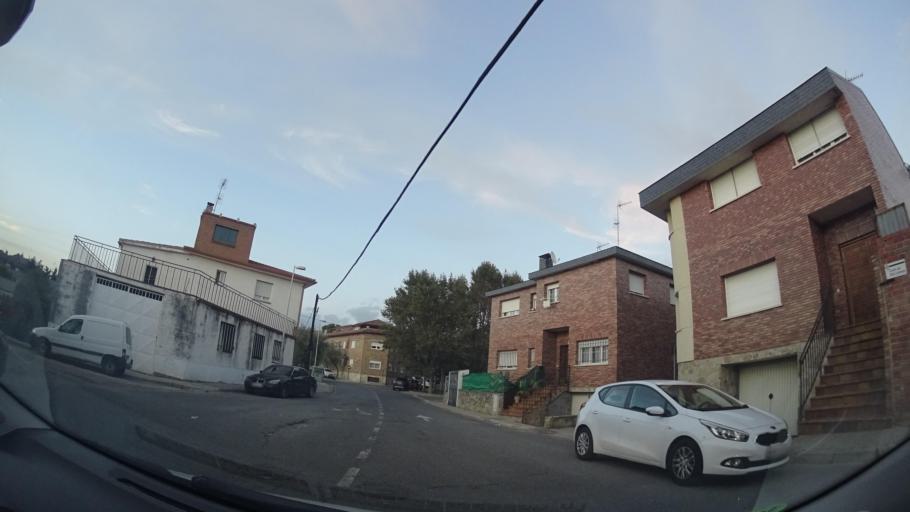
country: ES
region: Madrid
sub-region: Provincia de Madrid
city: Colmenarejo
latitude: 40.5627
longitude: -4.0174
